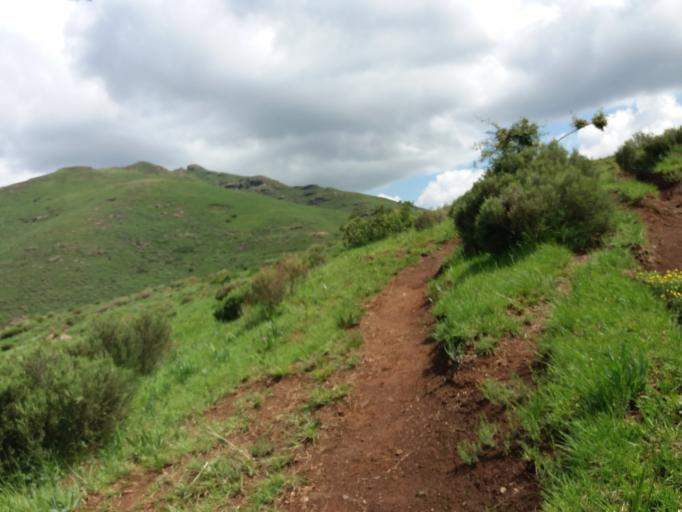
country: LS
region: Maseru
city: Nako
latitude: -29.6743
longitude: 27.9116
